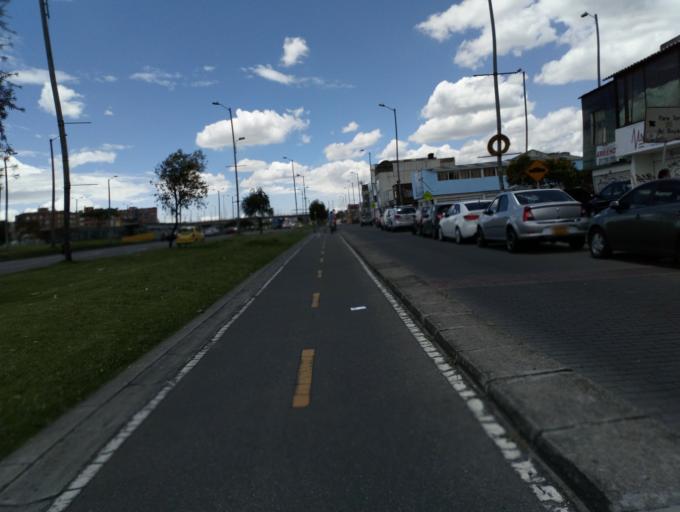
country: CO
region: Bogota D.C.
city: Bogota
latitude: 4.6305
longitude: -74.1325
